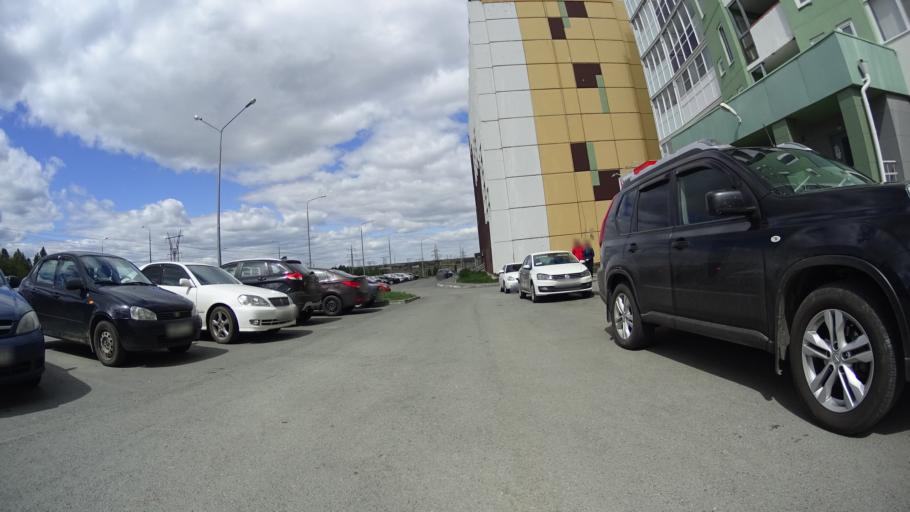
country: RU
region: Chelyabinsk
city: Roshchino
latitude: 55.1745
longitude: 61.2574
